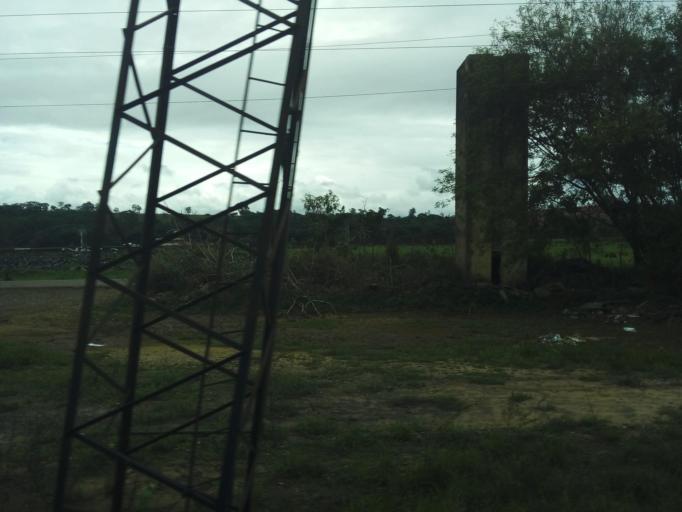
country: BR
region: Minas Gerais
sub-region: Ipatinga
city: Ipatinga
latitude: -19.4736
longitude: -42.4843
